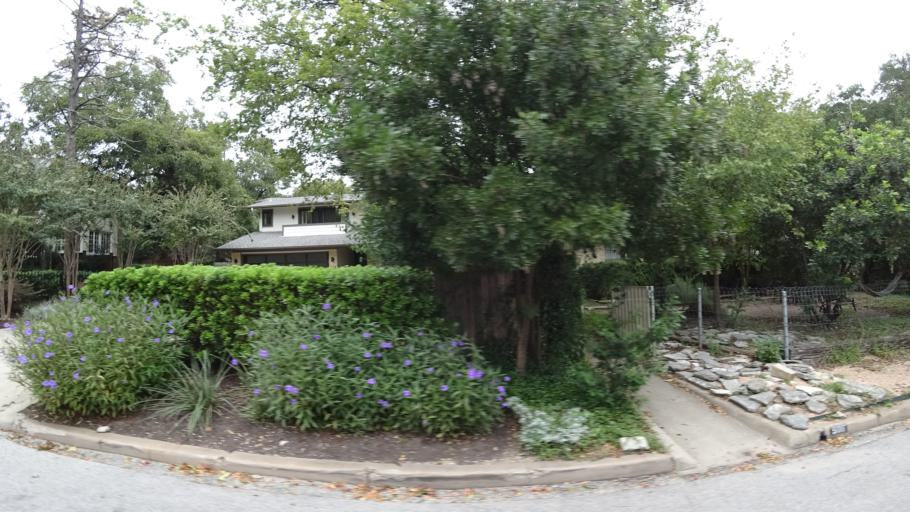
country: US
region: Texas
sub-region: Travis County
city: Austin
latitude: 30.2958
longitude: -97.7309
